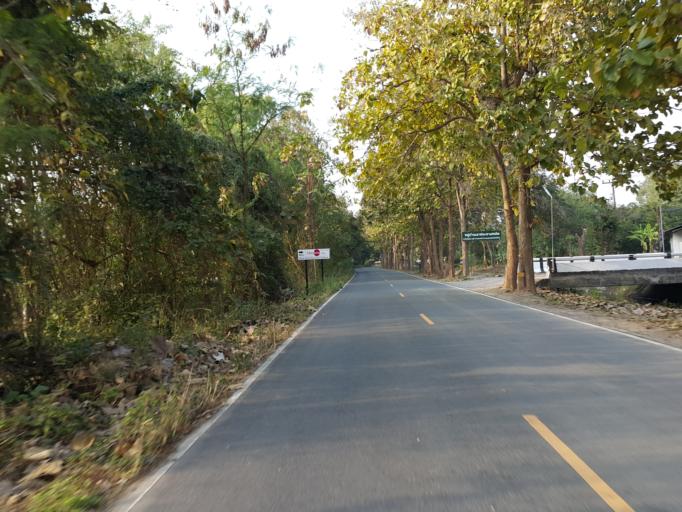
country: TH
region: Chiang Mai
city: San Sai
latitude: 18.8929
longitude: 99.1410
